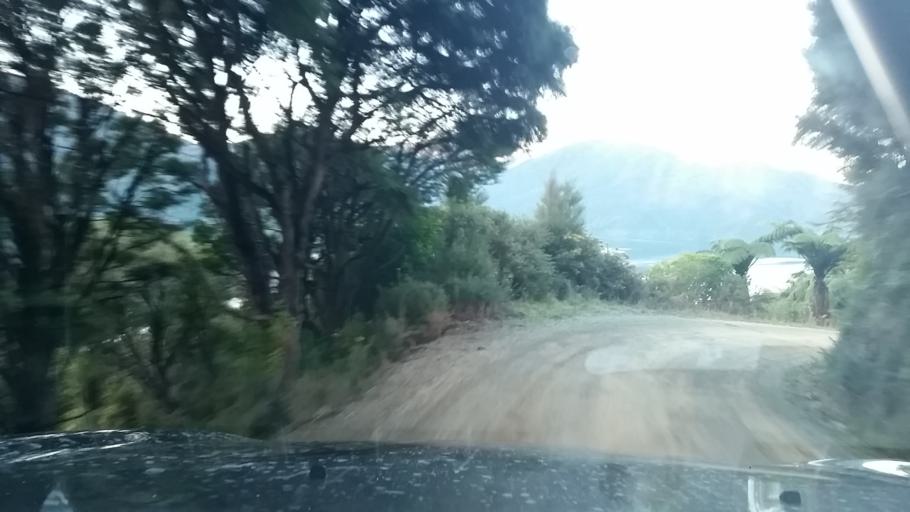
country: NZ
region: Marlborough
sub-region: Marlborough District
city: Picton
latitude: -41.1314
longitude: 174.1463
